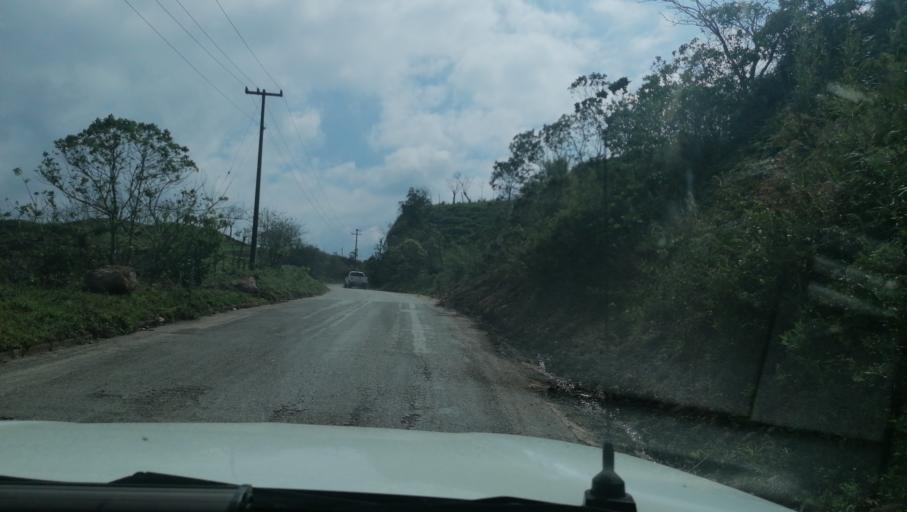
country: MX
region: Chiapas
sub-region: Ocotepec
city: San Pablo Huacano
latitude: 17.2520
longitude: -93.2677
